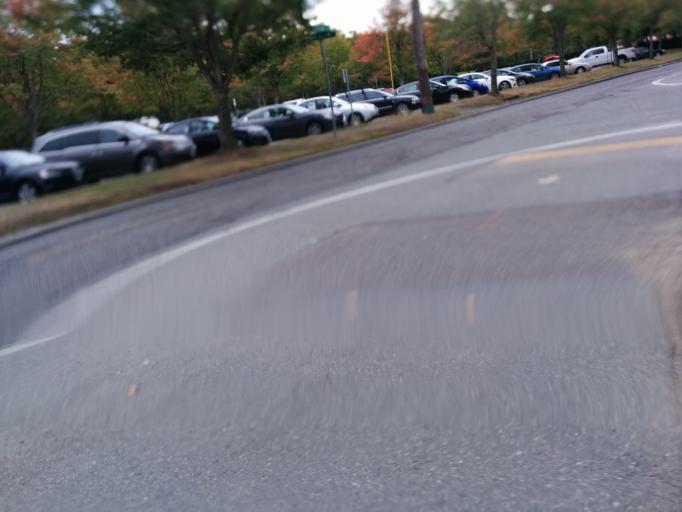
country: US
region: Washington
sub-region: King County
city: Seattle
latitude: 47.6469
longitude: -122.3350
